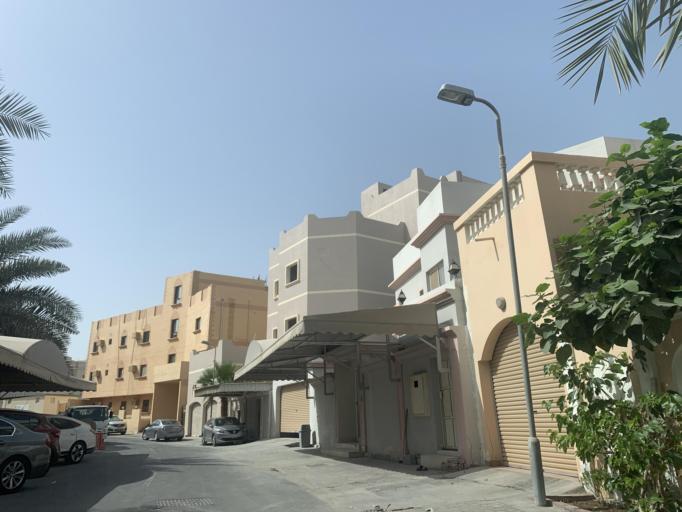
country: BH
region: Northern
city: Ar Rifa'
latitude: 26.1407
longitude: 50.5735
